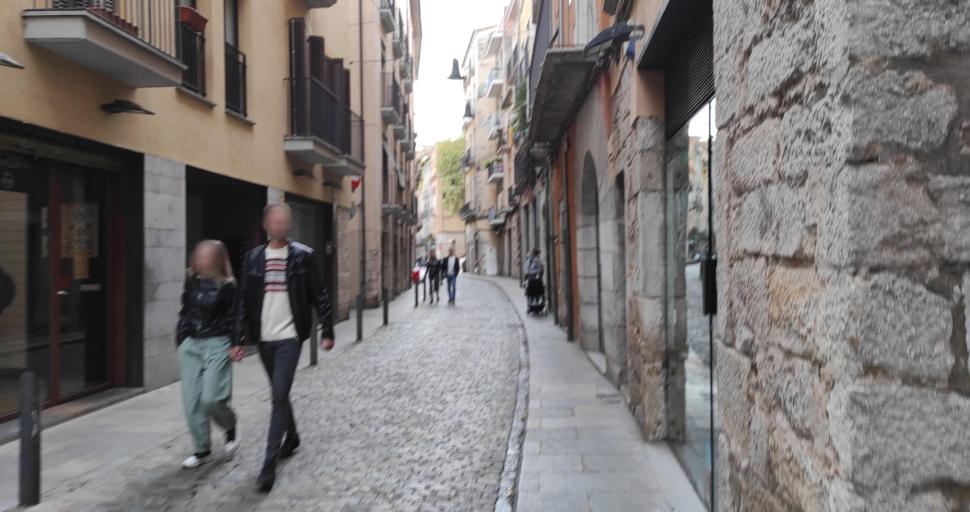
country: ES
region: Catalonia
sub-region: Provincia de Girona
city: Girona
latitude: 41.9888
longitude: 2.8245
